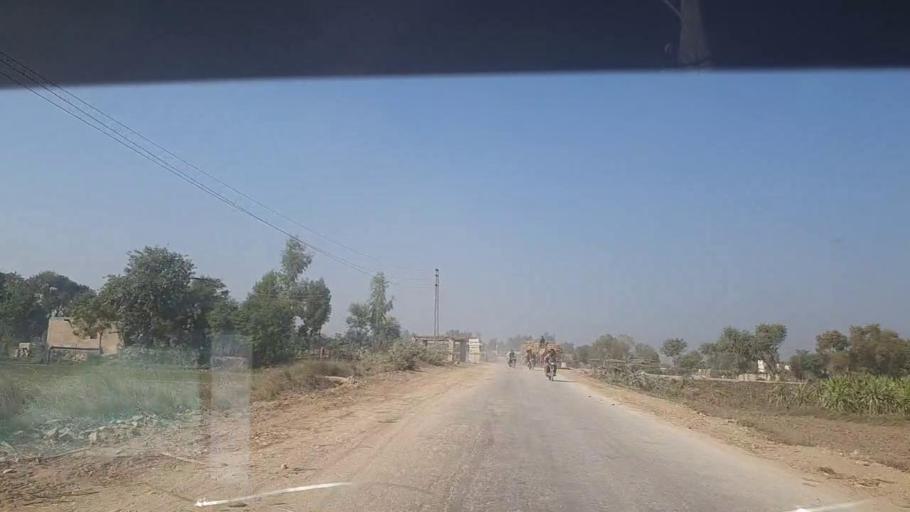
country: PK
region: Sindh
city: Kot Diji
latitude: 27.4286
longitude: 68.6543
